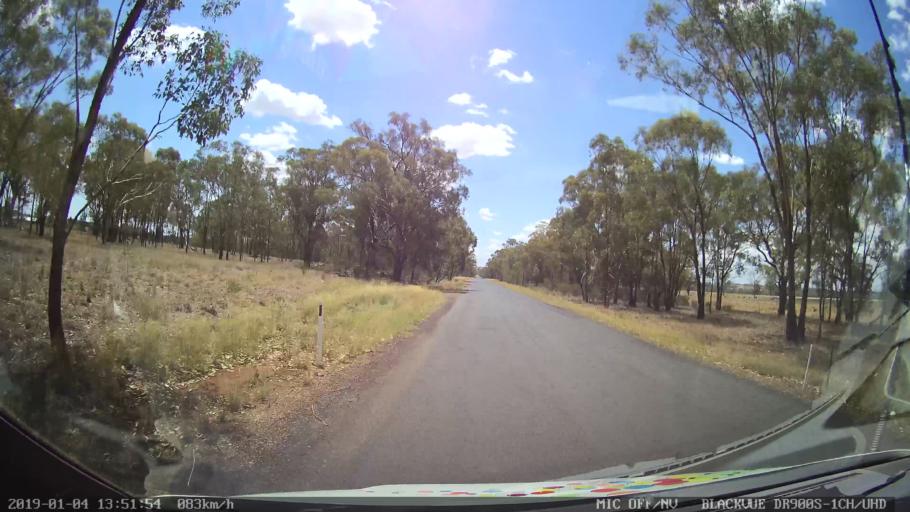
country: AU
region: New South Wales
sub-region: Dubbo Municipality
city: Dubbo
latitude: -32.4010
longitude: 148.5712
